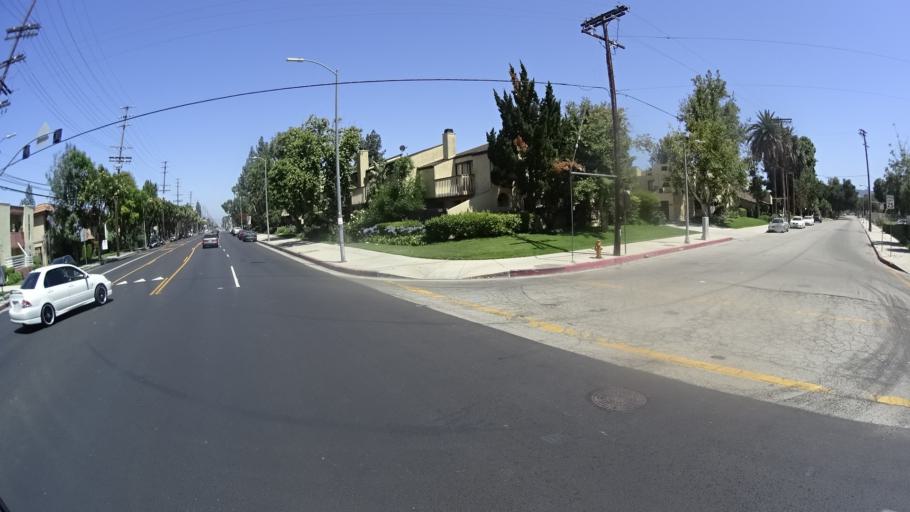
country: US
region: California
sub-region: Los Angeles County
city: Northridge
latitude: 34.1938
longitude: -118.5143
